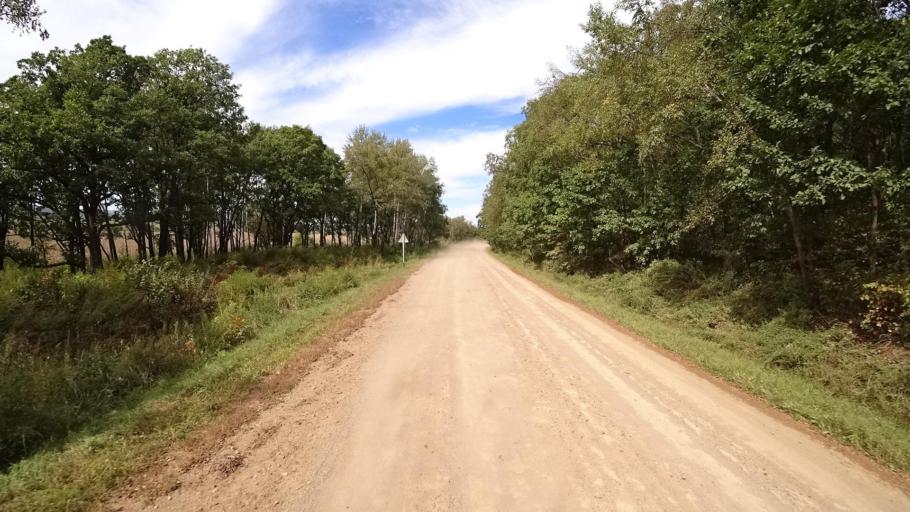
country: RU
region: Primorskiy
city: Yakovlevka
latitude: 44.5706
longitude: 133.5938
